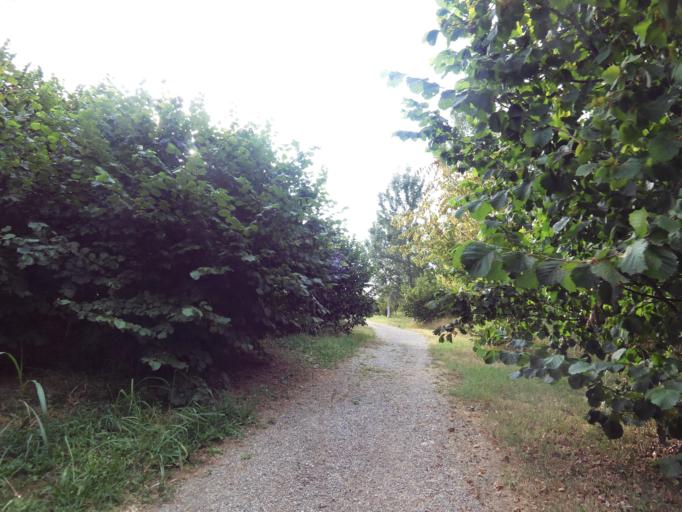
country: IT
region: Lombardy
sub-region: Citta metropolitana di Milano
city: San Giuliano Milanese
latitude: 45.3869
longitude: 9.2944
